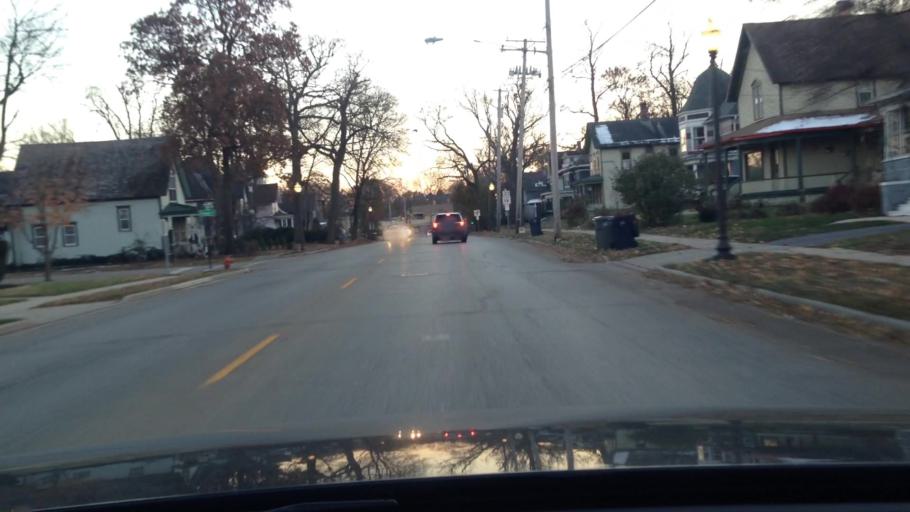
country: US
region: Illinois
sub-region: Kane County
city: Elgin
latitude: 42.0394
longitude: -88.2676
